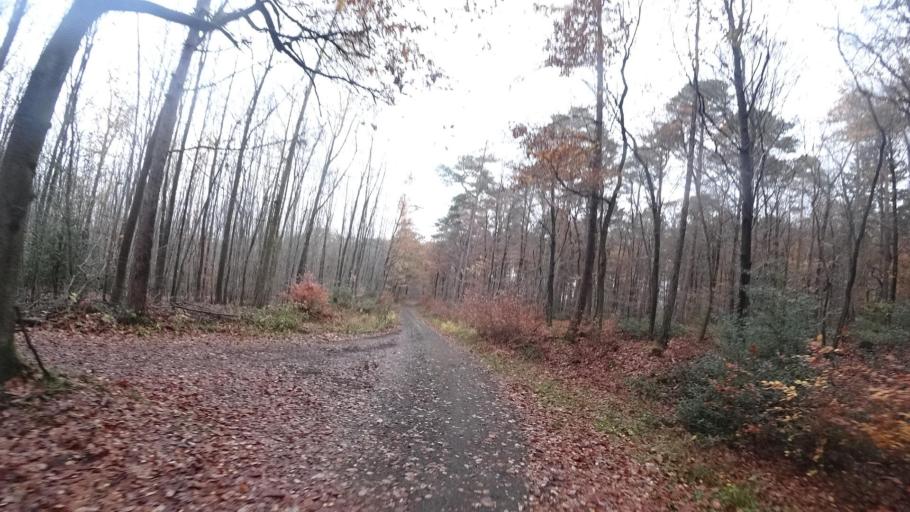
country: DE
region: Rheinland-Pfalz
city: Bad Neuenahr-Ahrweiler
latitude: 50.5291
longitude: 7.1252
